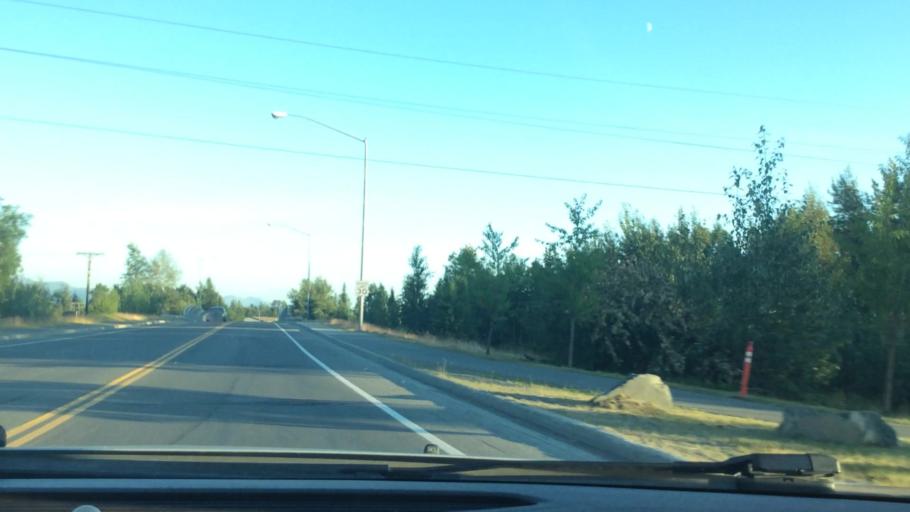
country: US
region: Alaska
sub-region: Anchorage Municipality
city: Anchorage
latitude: 61.2260
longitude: -149.7917
